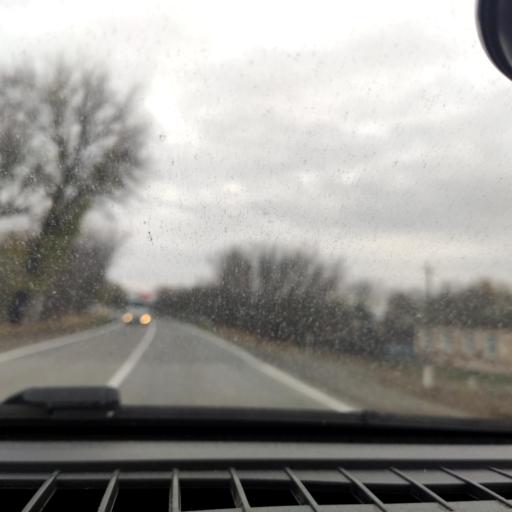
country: RU
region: Voronezj
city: Ostrogozhsk
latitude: 50.7921
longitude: 38.9571
